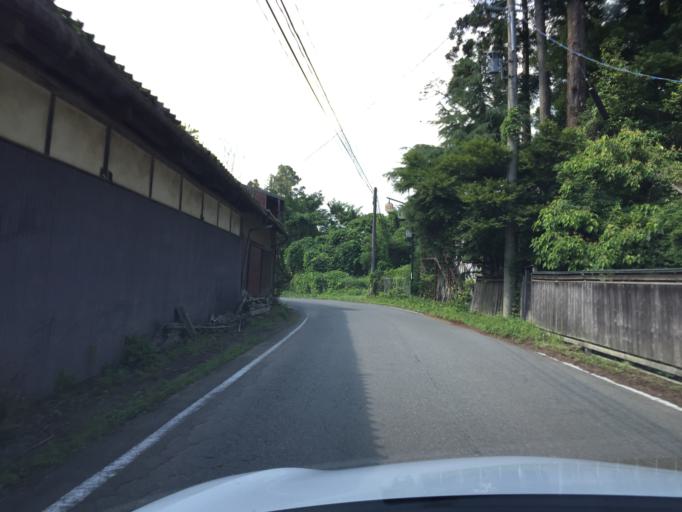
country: JP
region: Ibaraki
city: Kitaibaraki
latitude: 36.9742
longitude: 140.7035
